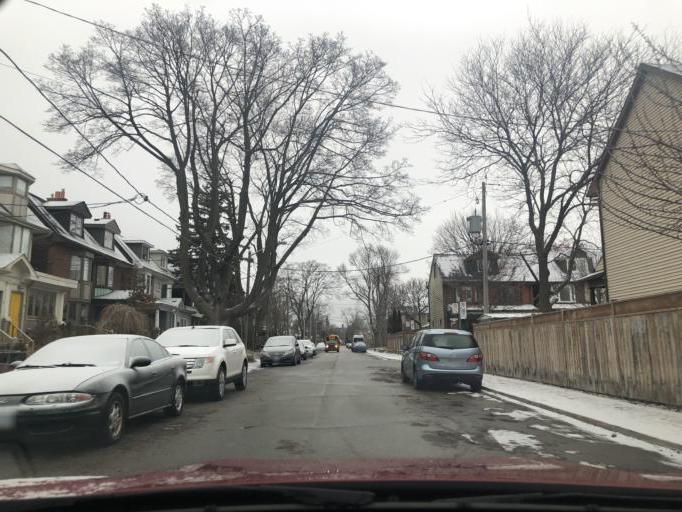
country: CA
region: Ontario
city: Toronto
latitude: 43.6822
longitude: -79.3402
